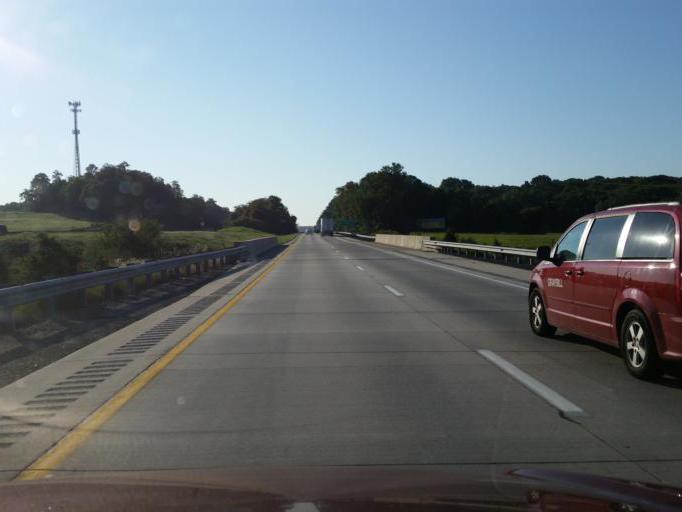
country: US
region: Pennsylvania
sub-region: Lancaster County
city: Elizabethtown
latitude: 40.1920
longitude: -76.6298
